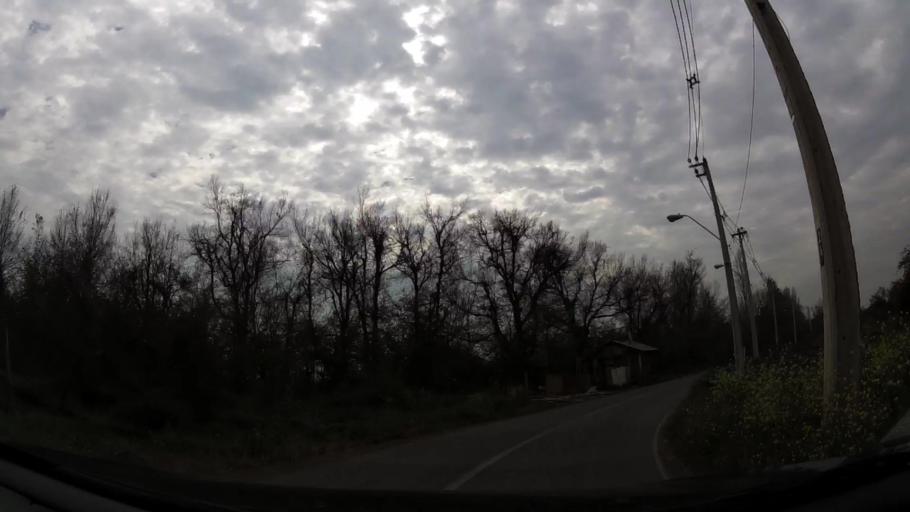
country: CL
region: Santiago Metropolitan
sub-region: Provincia de Chacabuco
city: Lampa
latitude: -33.2235
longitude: -70.7715
